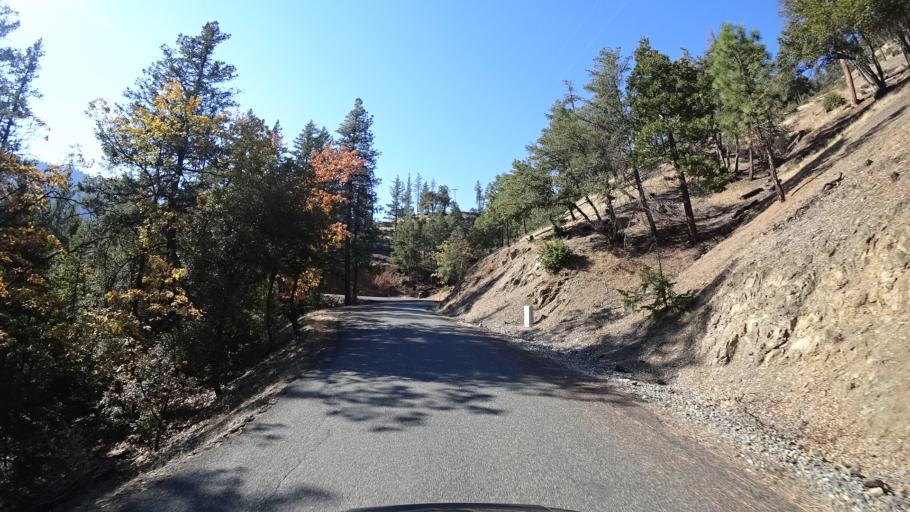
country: US
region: California
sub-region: Siskiyou County
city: Happy Camp
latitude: 41.7112
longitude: -123.0283
